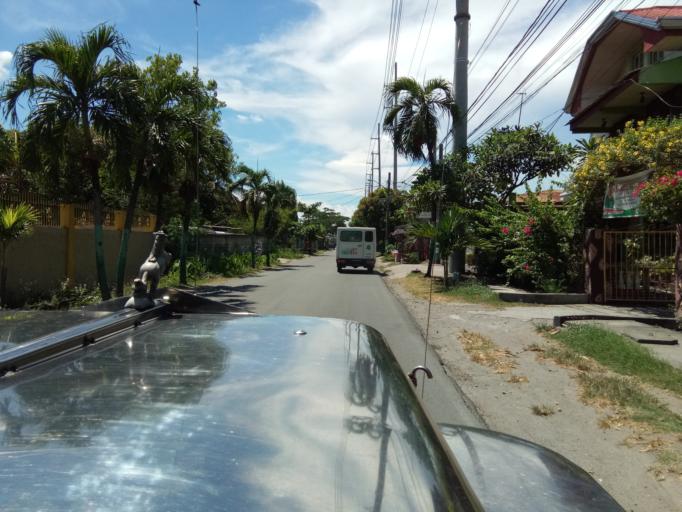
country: PH
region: Calabarzon
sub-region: Province of Cavite
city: Pasong Kawayan Primero
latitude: 14.3599
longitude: 120.8968
